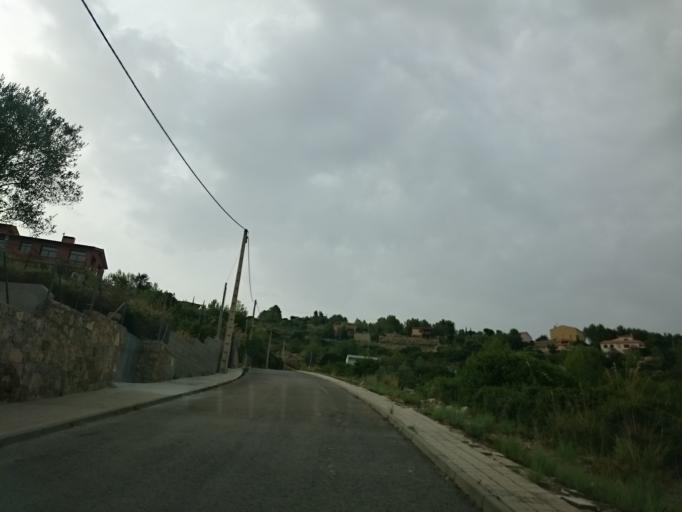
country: ES
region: Catalonia
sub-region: Provincia de Barcelona
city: Olivella
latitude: 41.2925
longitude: 1.8592
